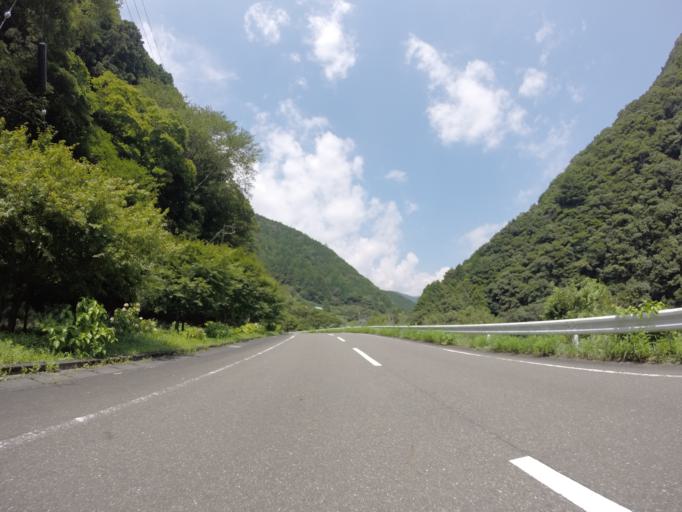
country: JP
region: Shizuoka
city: Shizuoka-shi
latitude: 35.2235
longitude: 138.3505
